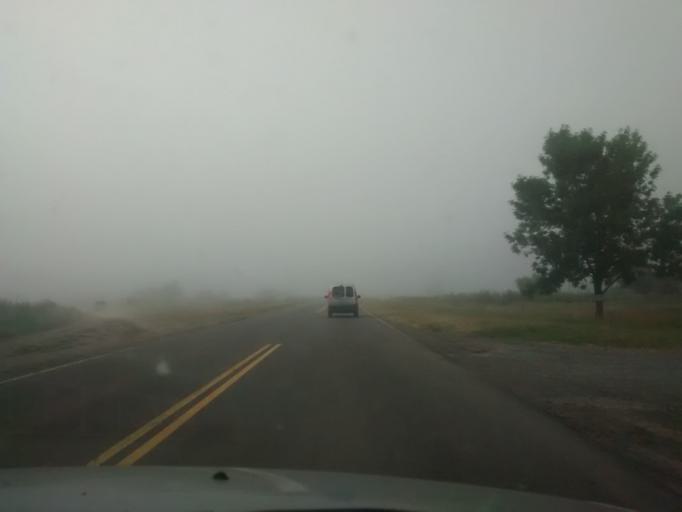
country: AR
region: Buenos Aires
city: Ranchos
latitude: -35.3630
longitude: -58.2503
